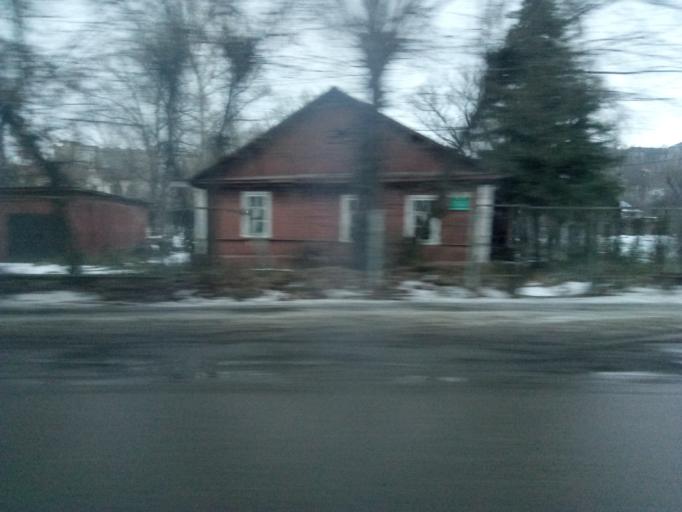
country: RU
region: Tula
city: Tula
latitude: 54.1945
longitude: 37.5758
